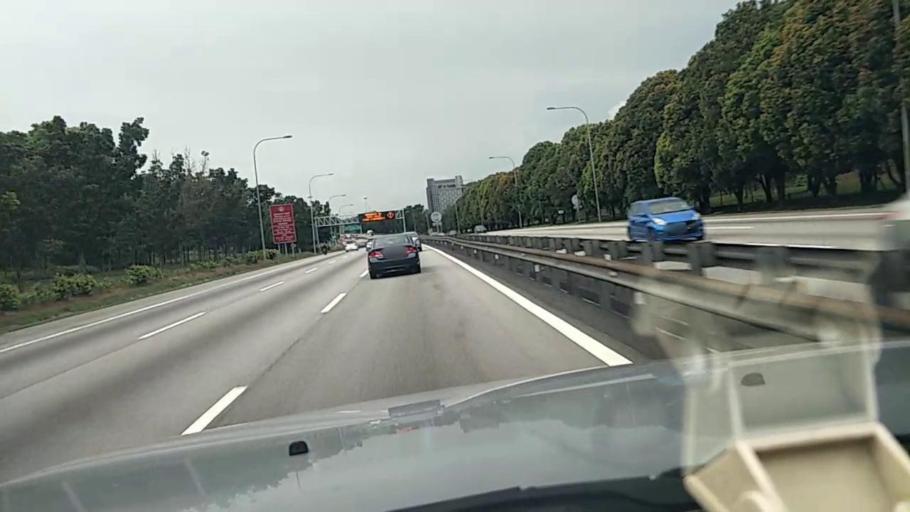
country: MY
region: Selangor
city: Subang Jaya
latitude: 3.0122
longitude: 101.5805
